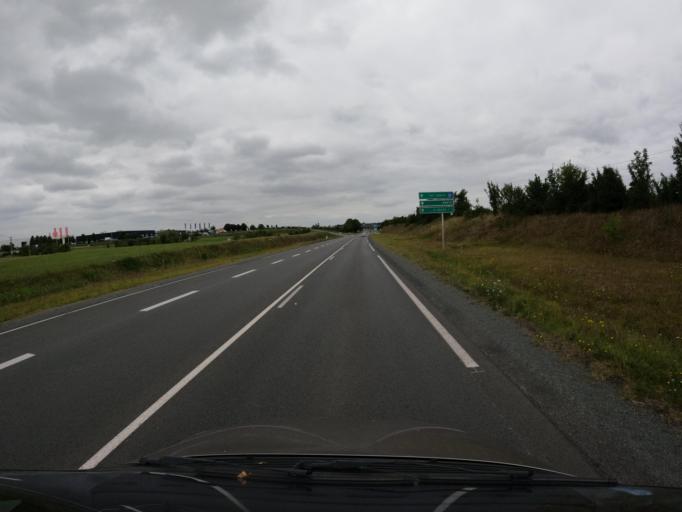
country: FR
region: Pays de la Loire
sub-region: Departement de la Vendee
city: Fontenay-le-Comte
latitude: 46.4461
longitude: -0.8092
